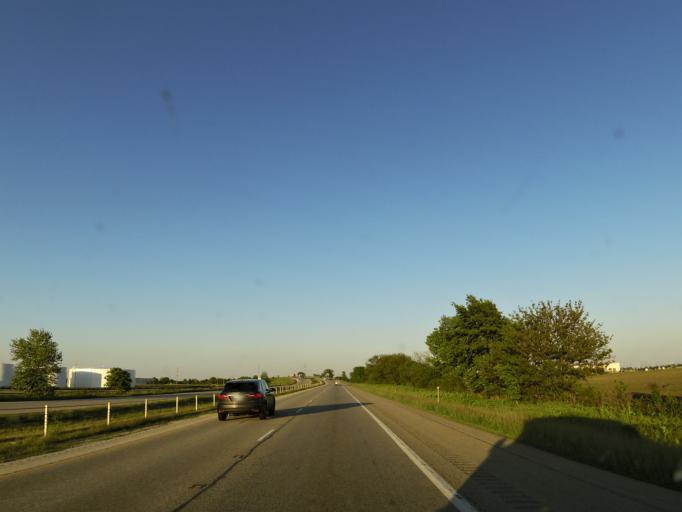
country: US
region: Illinois
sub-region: Vermilion County
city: Danville
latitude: 40.1156
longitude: -87.5505
